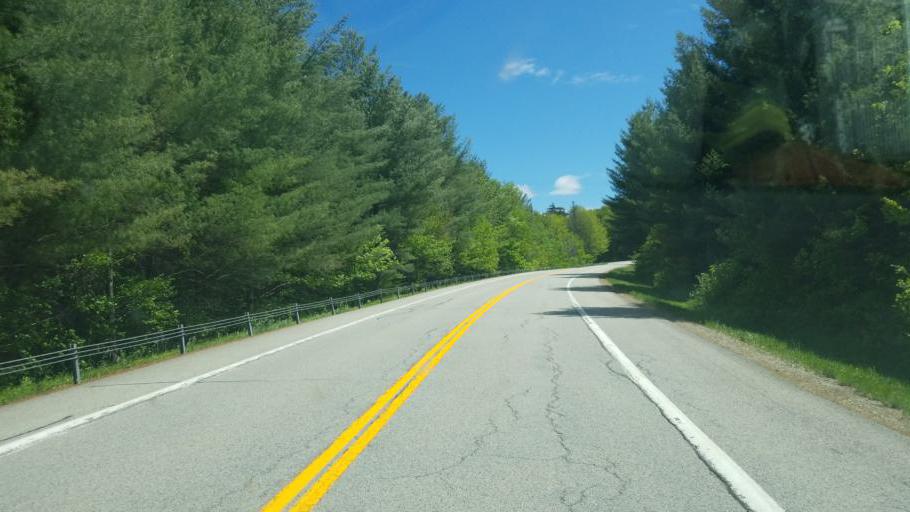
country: US
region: New York
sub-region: Hamilton County
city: Lake Pleasant
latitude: 43.2746
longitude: -74.5513
